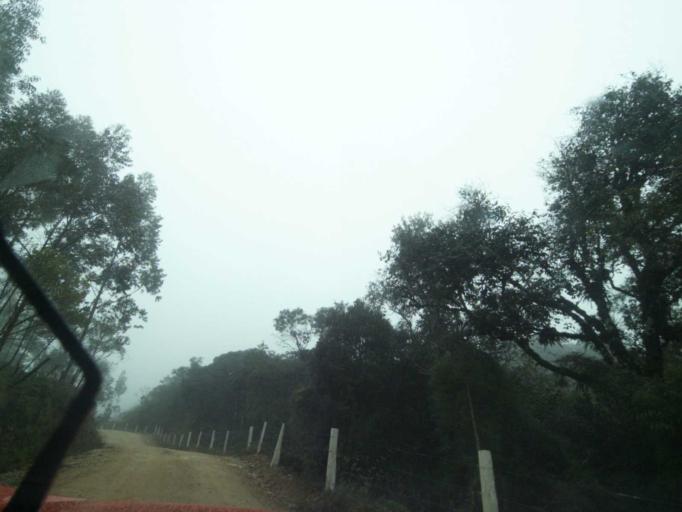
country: BR
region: Santa Catarina
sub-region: Anitapolis
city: Anitapolis
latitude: -27.9035
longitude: -49.1627
